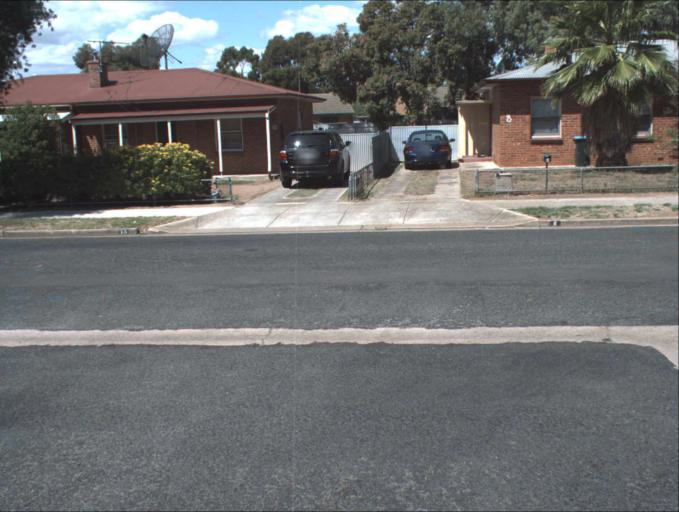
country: AU
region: South Australia
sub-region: Port Adelaide Enfield
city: Blair Athol
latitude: -34.8589
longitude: 138.5885
